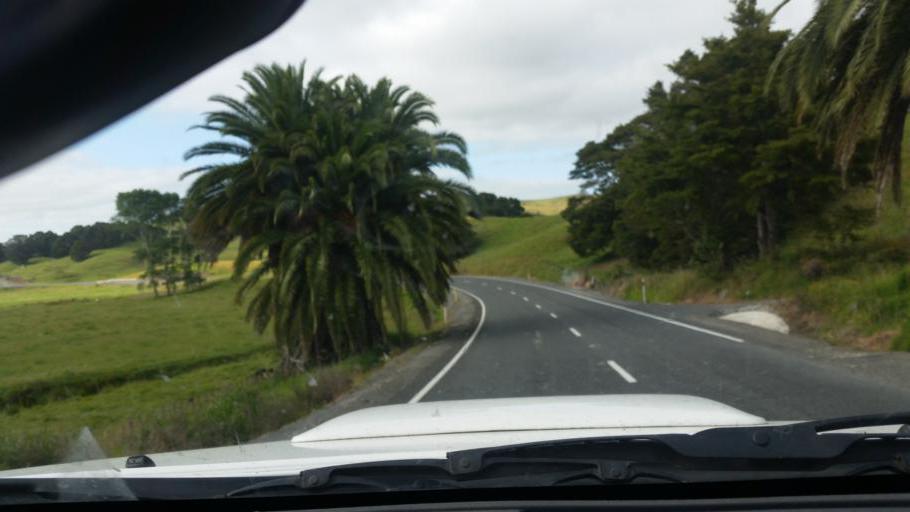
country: NZ
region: Northland
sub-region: Kaipara District
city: Dargaville
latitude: -35.8457
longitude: 173.8438
